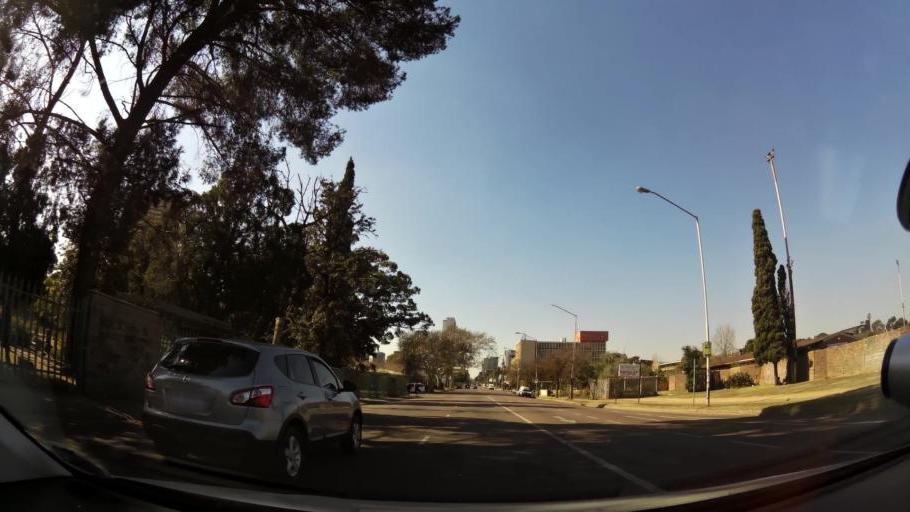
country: ZA
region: Gauteng
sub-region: City of Tshwane Metropolitan Municipality
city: Pretoria
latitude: -25.7472
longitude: 28.1767
